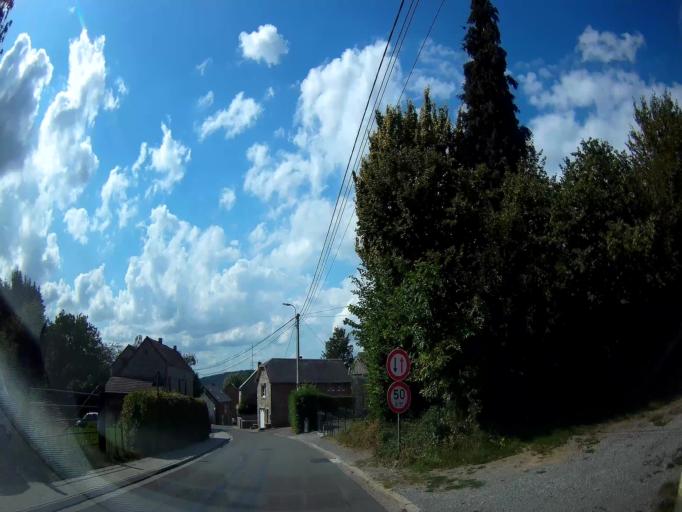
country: BE
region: Wallonia
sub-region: Province de Namur
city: Yvoir
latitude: 50.3540
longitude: 4.8971
